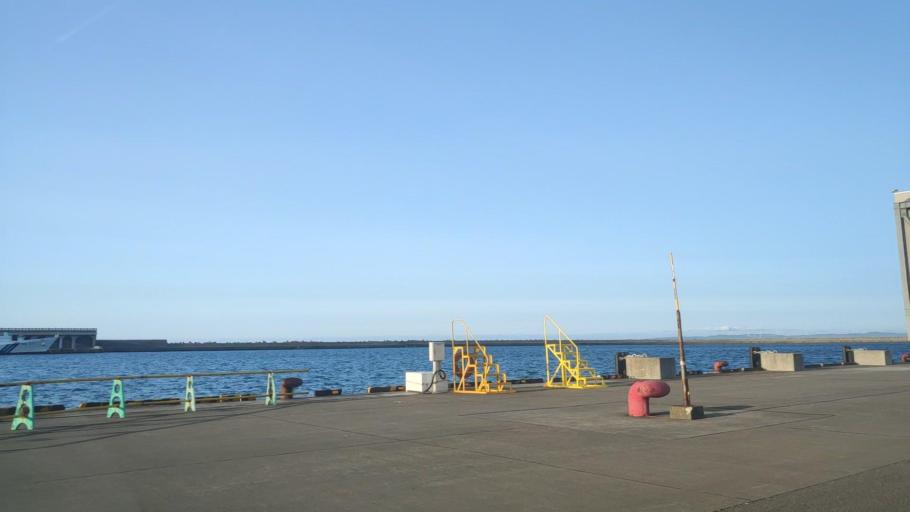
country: JP
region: Hokkaido
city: Wakkanai
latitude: 45.4161
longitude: 141.6819
